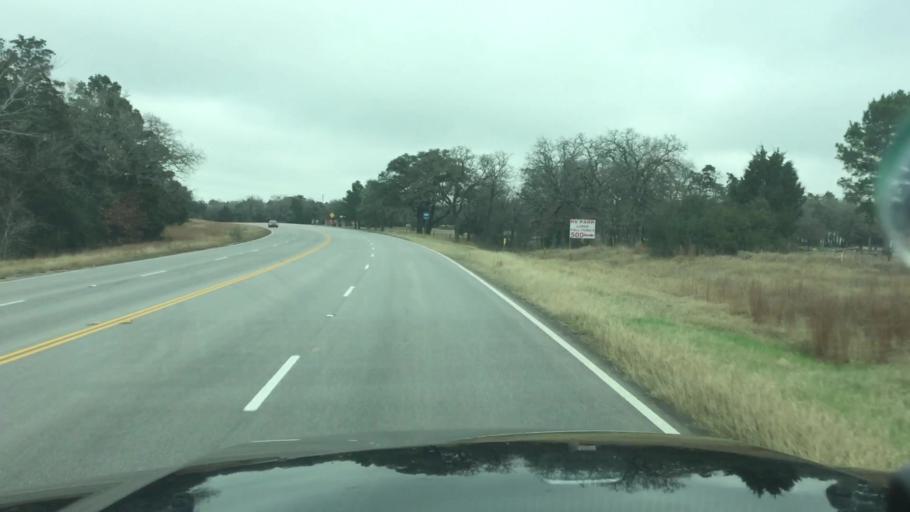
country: US
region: Texas
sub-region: Lee County
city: Giddings
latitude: 30.0927
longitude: -96.9130
